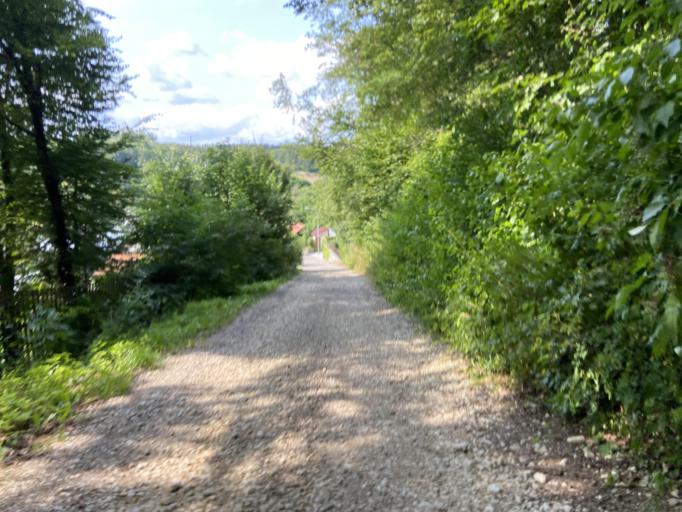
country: DE
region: Baden-Wuerttemberg
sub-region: Tuebingen Region
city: Scheer
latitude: 48.0818
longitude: 9.2775
